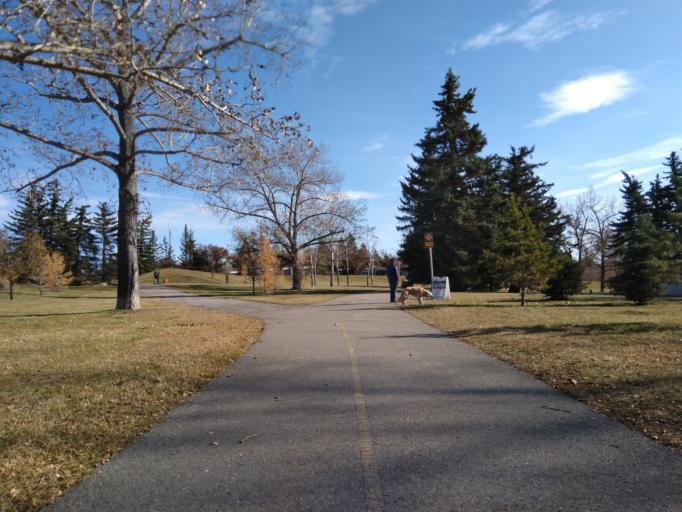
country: CA
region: Alberta
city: Calgary
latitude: 51.0893
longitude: -114.0964
